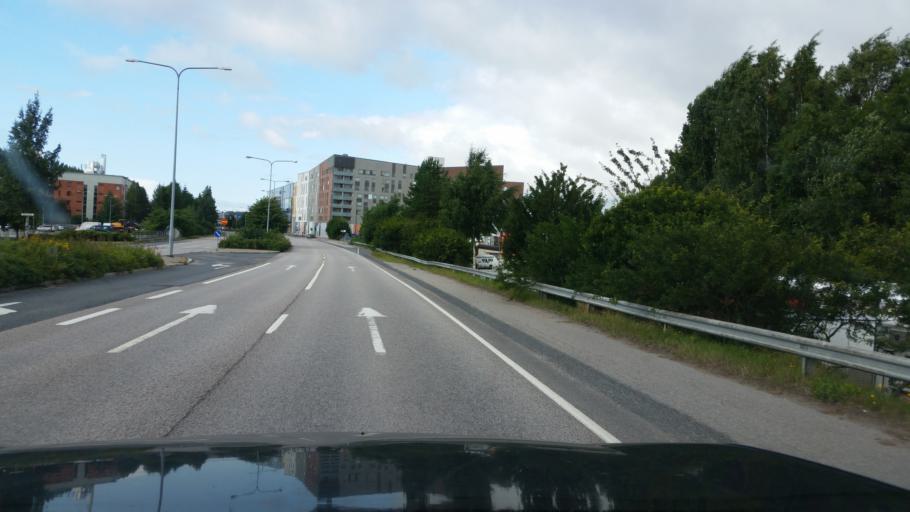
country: FI
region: Uusimaa
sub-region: Helsinki
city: Vantaa
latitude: 60.2157
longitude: 25.0947
